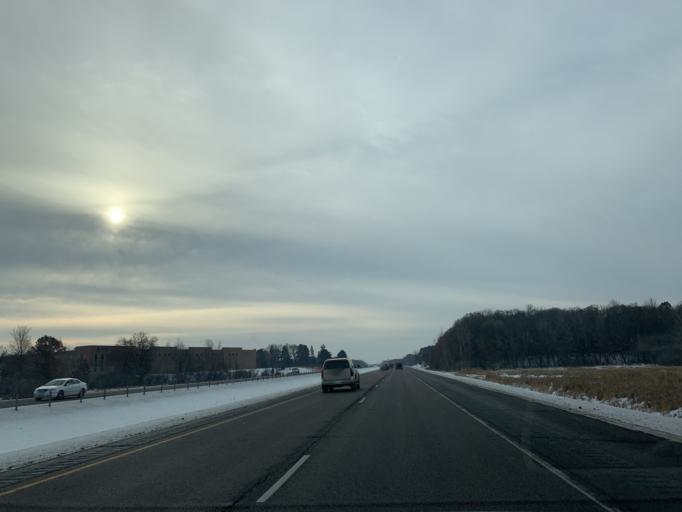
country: US
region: Minnesota
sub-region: Chisago County
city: Wyoming
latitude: 45.3195
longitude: -93.0036
